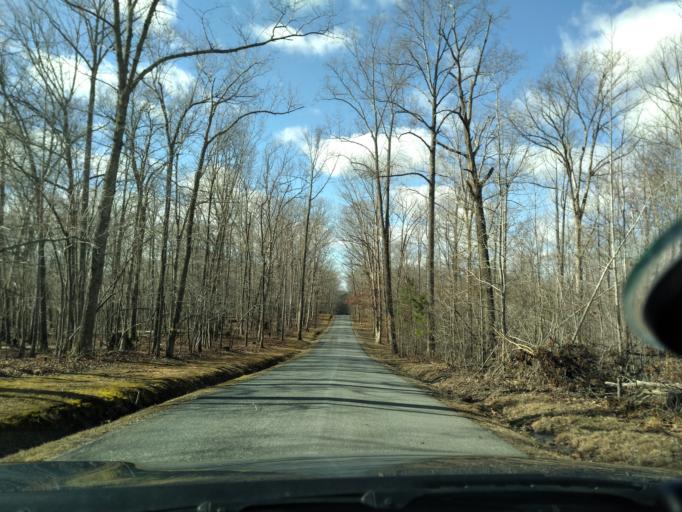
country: US
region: Virginia
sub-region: Nottoway County
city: Crewe
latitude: 37.1786
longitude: -78.2671
